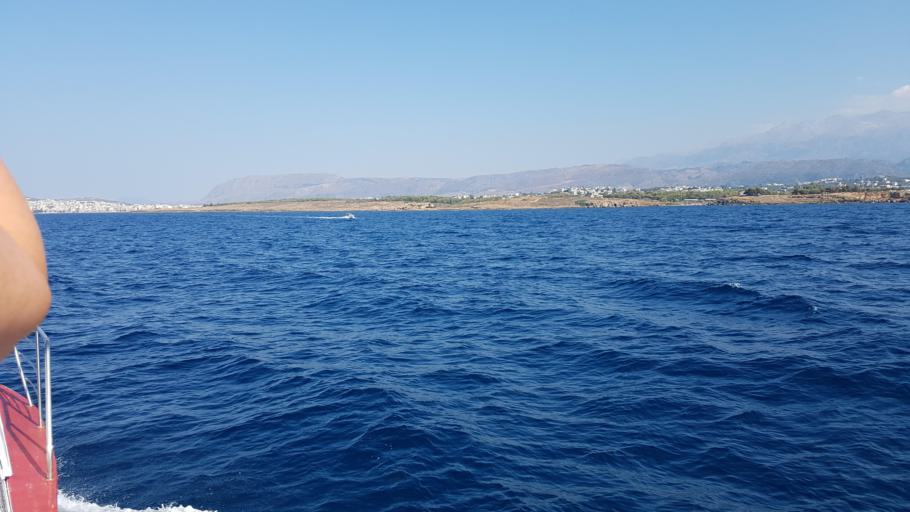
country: GR
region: Crete
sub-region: Nomos Chanias
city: Daratsos
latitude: 35.5227
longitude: 23.9741
